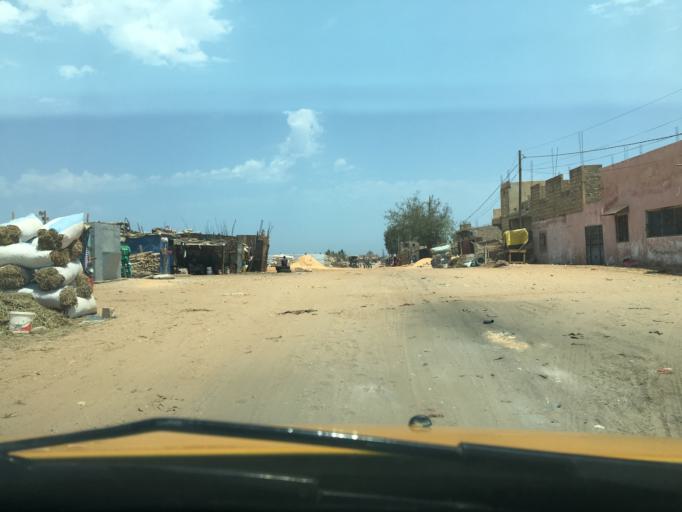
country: SN
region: Thies
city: Thies
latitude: 14.8036
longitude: -17.1855
